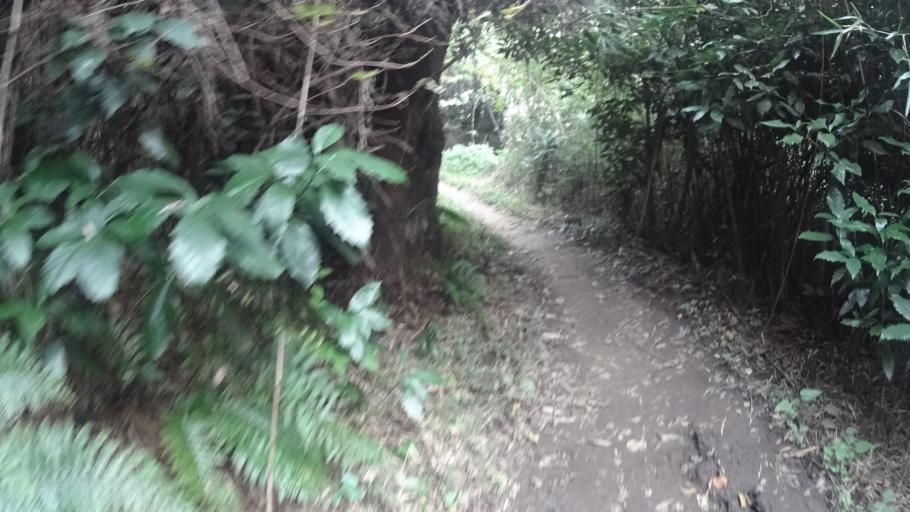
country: JP
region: Kanagawa
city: Zushi
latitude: 35.2923
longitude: 139.6044
